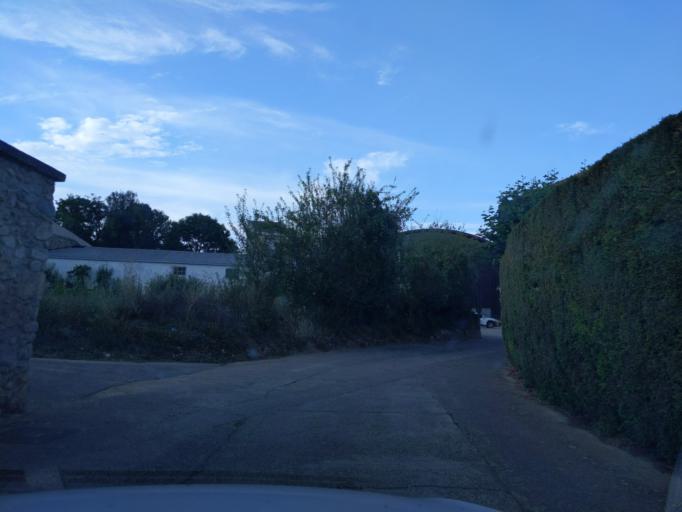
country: ES
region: La Rioja
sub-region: Provincia de La Rioja
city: Santurdejo
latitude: 42.3901
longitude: -2.9817
